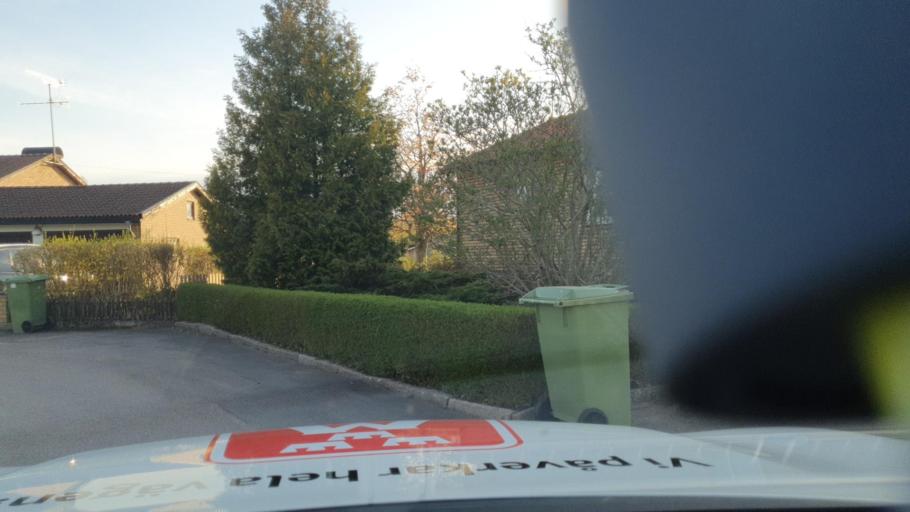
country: SE
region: OEstergoetland
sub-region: Linkopings Kommun
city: Vikingstad
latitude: 58.3788
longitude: 15.4321
